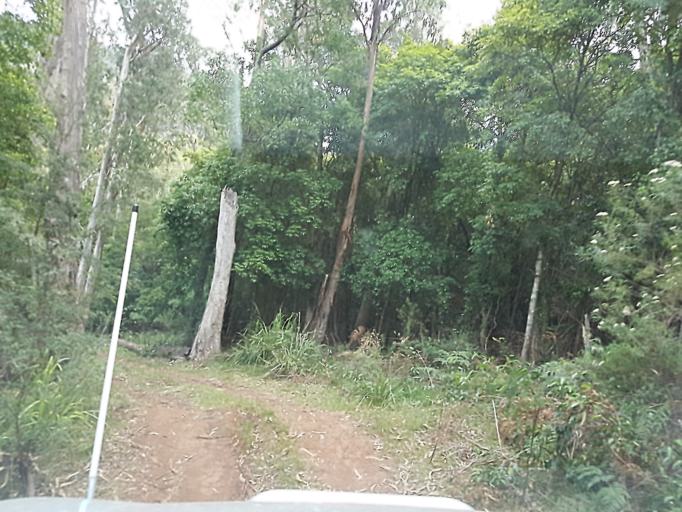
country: AU
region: Victoria
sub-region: East Gippsland
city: Lakes Entrance
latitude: -37.3648
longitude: 148.3517
